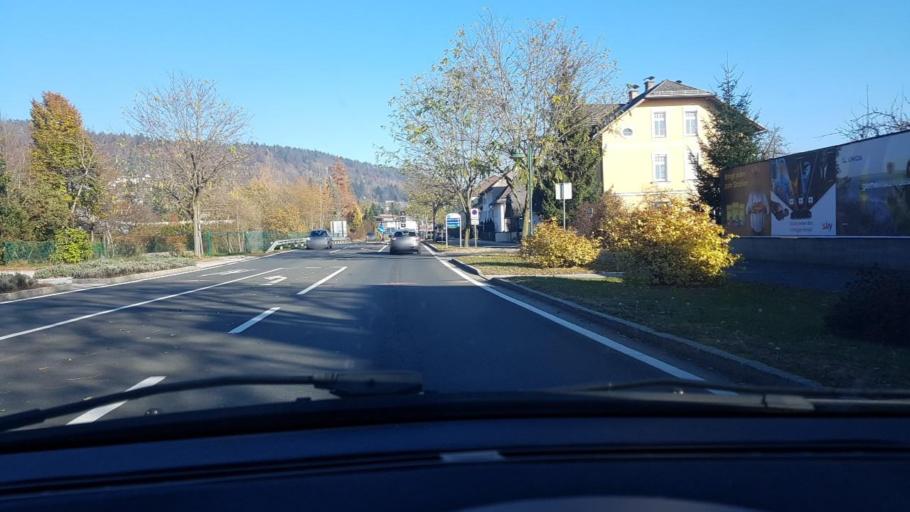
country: AT
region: Carinthia
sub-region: Politischer Bezirk Klagenfurt Land
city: Keutschach am See
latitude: 46.6259
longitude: 14.2051
